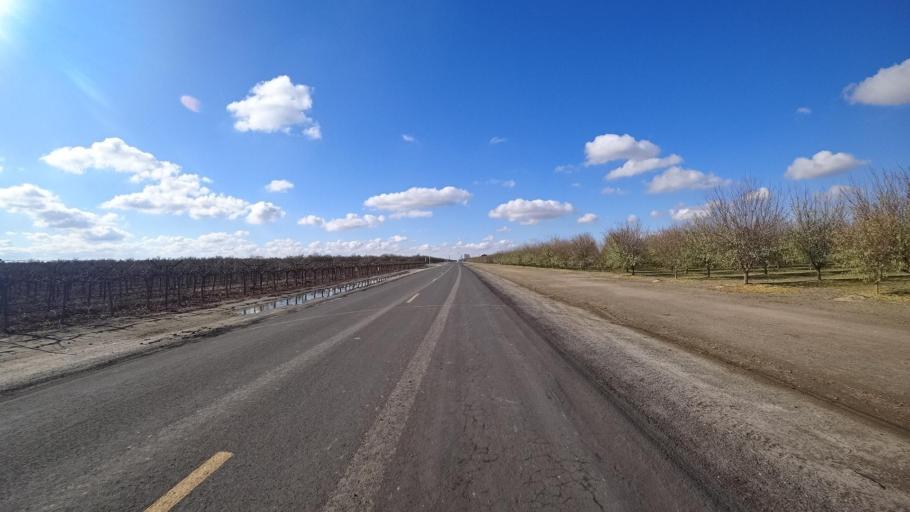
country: US
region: California
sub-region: Kern County
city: Delano
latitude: 35.7323
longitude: -119.3057
